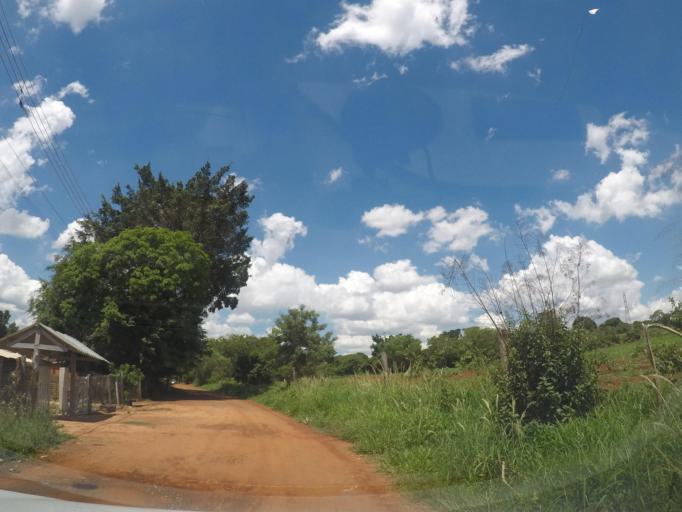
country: BR
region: Sao Paulo
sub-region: Sumare
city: Sumare
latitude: -22.8381
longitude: -47.2424
